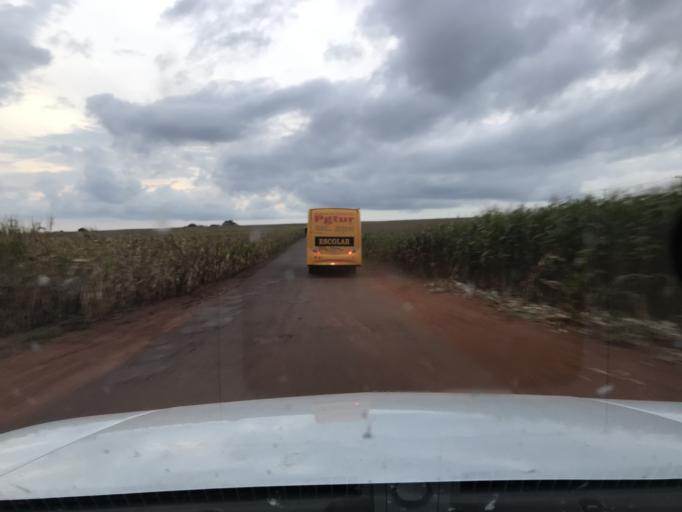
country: BR
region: Parana
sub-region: Palotina
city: Palotina
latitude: -24.2479
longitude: -53.7924
